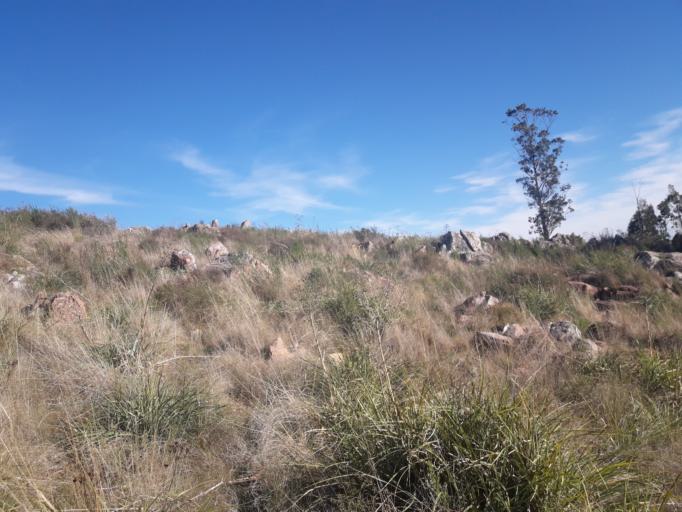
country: AR
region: Buenos Aires
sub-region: Partido de Tandil
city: Tandil
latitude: -37.3439
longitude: -59.1216
